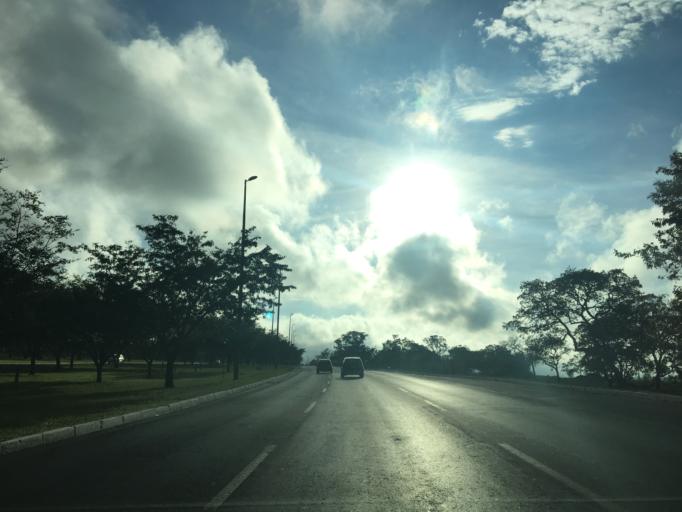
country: BR
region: Federal District
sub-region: Brasilia
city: Brasilia
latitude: -15.8130
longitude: -47.8667
